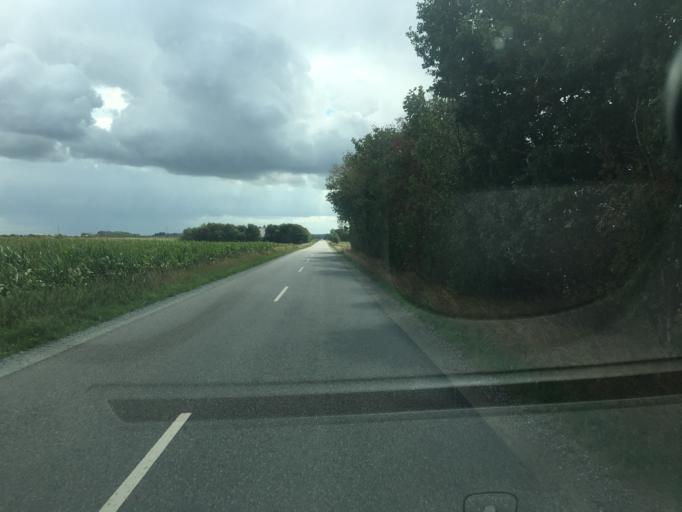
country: DK
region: South Denmark
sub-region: Tonder Kommune
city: Logumkloster
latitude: 55.0464
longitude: 8.9612
